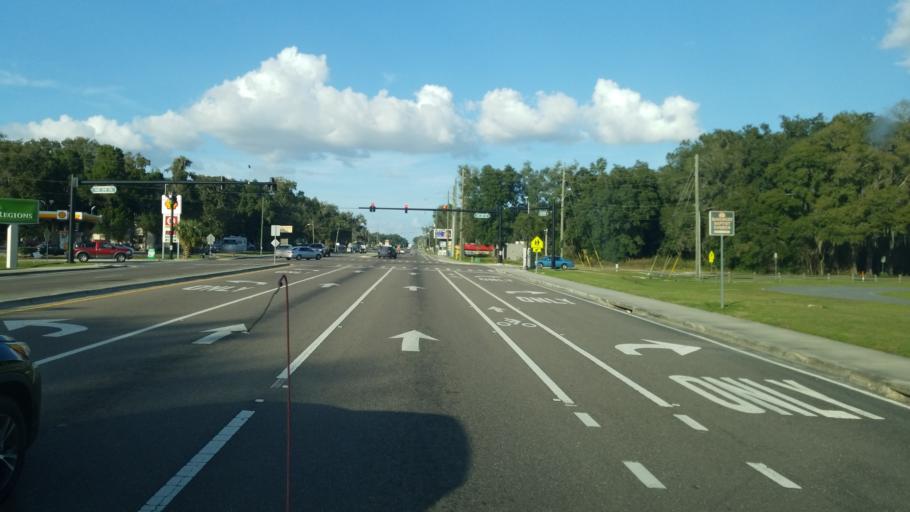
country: US
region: Florida
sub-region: Marion County
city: Ocala
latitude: 29.2146
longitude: -82.1262
